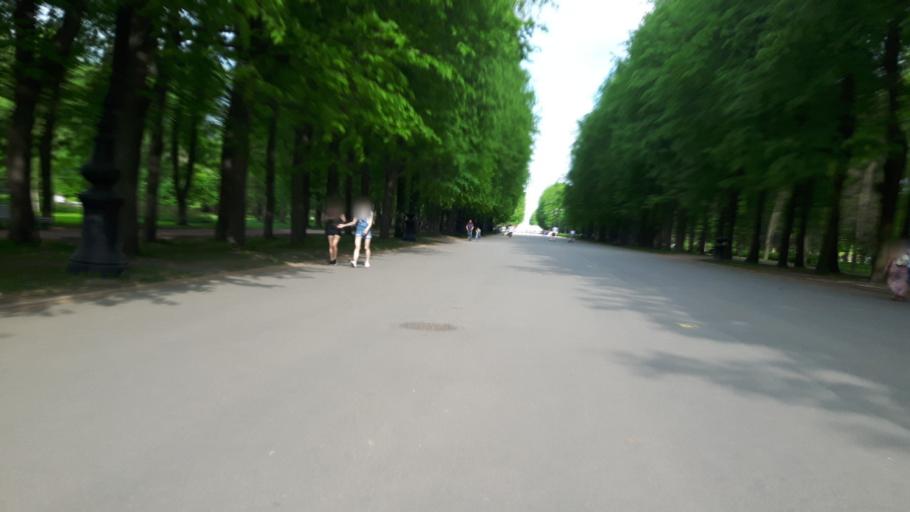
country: RU
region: St.-Petersburg
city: Staraya Derevnya
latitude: 59.9725
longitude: 30.2312
